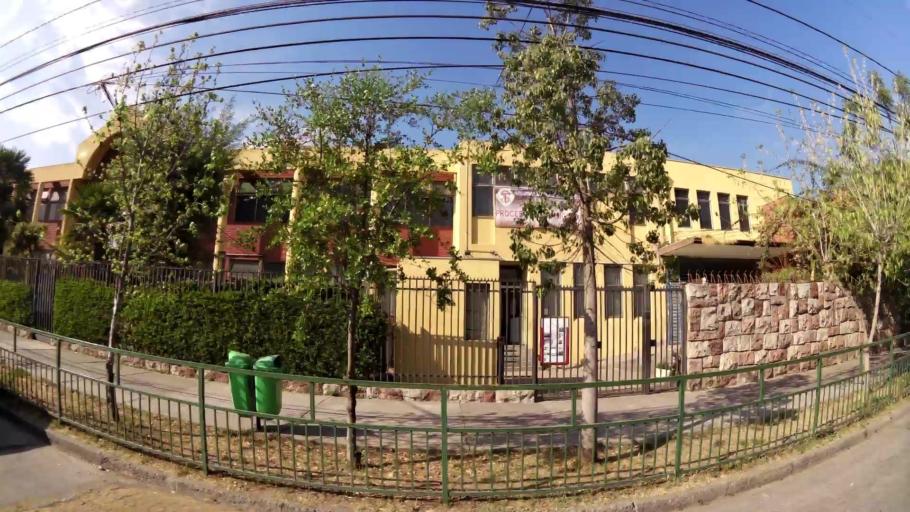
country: CL
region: Santiago Metropolitan
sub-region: Provincia de Santiago
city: La Pintana
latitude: -33.5579
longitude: -70.5923
